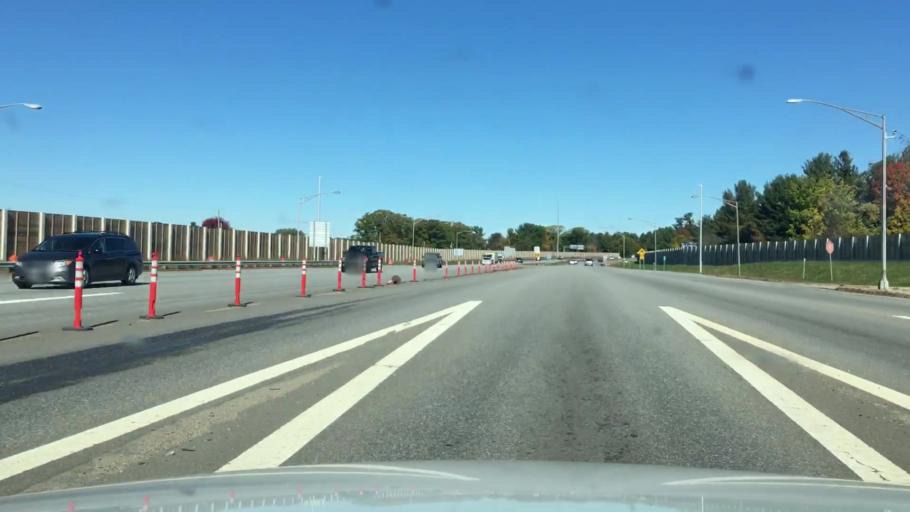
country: US
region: Maine
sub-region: York County
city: Eliot
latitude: 43.1369
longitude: -70.8414
